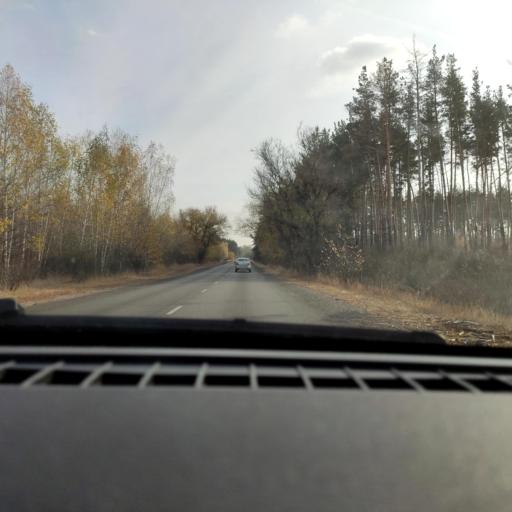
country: RU
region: Voronezj
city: Maslovka
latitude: 51.5799
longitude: 39.2857
